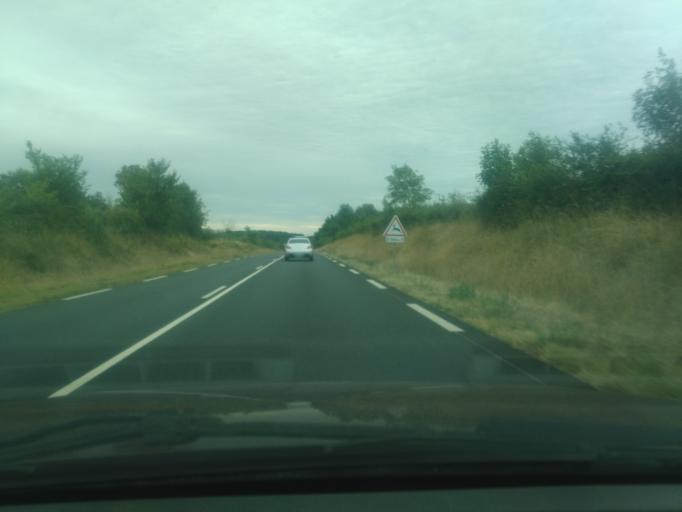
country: FR
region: Centre
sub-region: Departement de l'Indre
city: Le Pechereau
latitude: 46.5946
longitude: 1.5663
